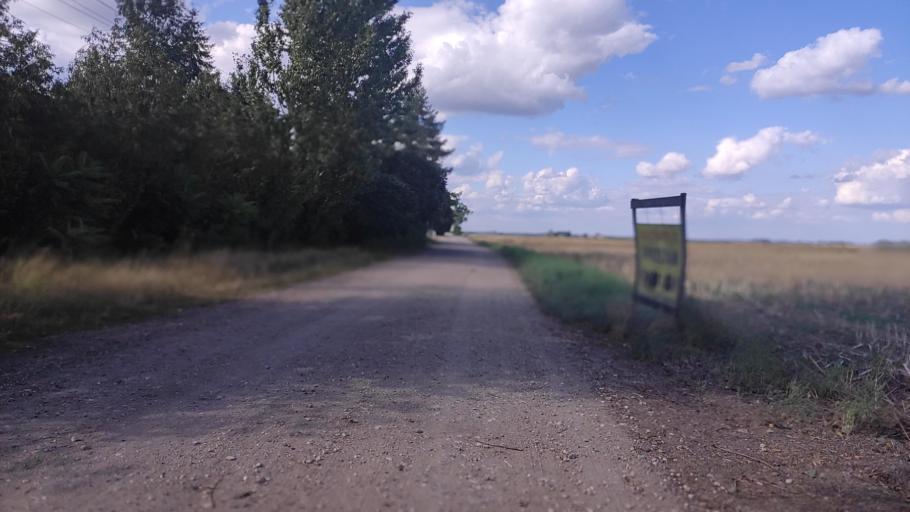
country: PL
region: Greater Poland Voivodeship
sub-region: Powiat poznanski
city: Swarzedz
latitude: 52.4159
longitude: 17.1409
